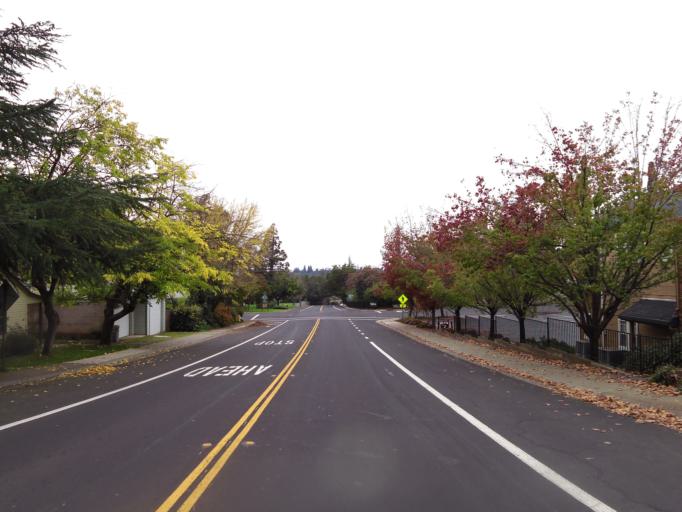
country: US
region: California
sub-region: Sacramento County
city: Folsom
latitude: 38.6727
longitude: -121.1787
